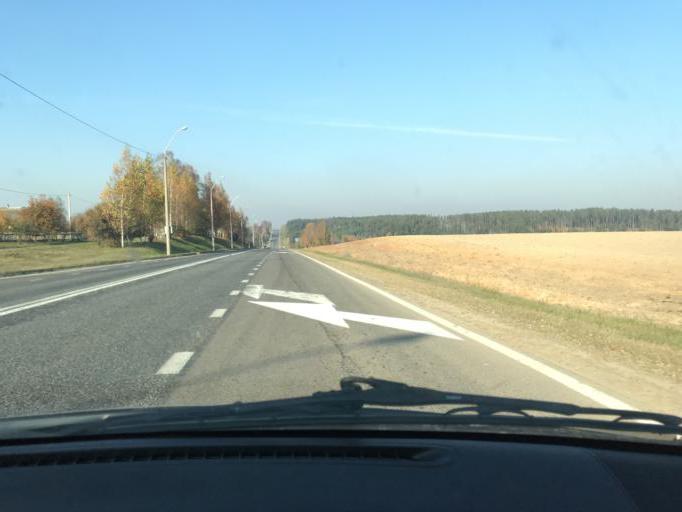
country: BY
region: Vitebsk
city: Orsha
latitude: 54.3789
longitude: 30.4441
